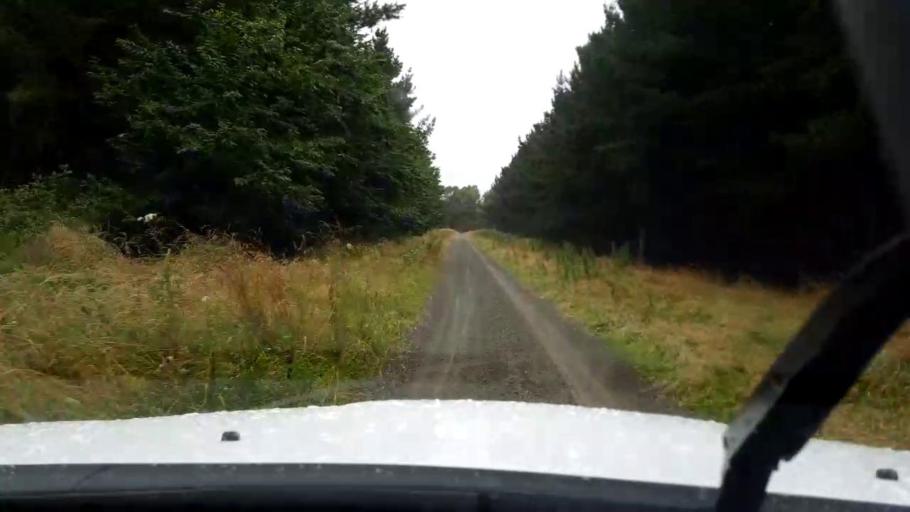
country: NZ
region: Canterbury
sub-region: Timaru District
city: Pleasant Point
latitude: -44.1832
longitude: 171.1021
